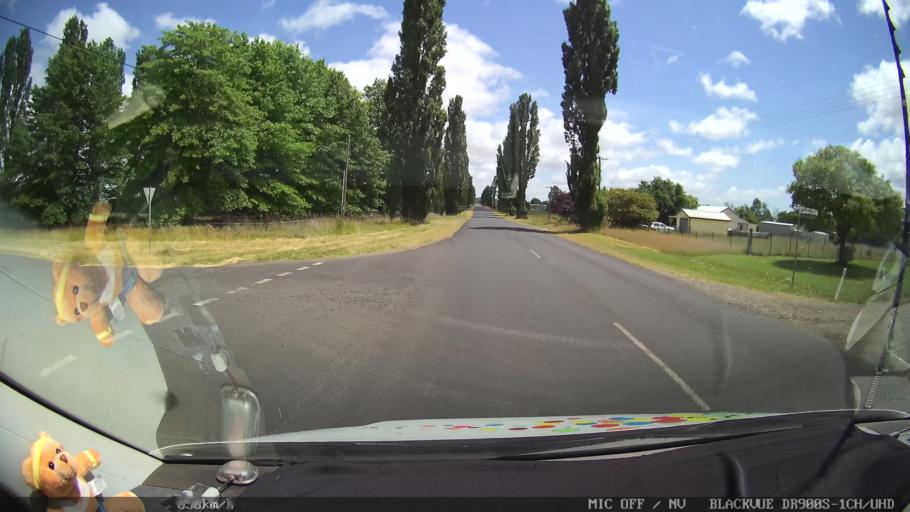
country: AU
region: New South Wales
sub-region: Glen Innes Severn
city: Glen Innes
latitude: -29.7268
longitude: 151.7255
